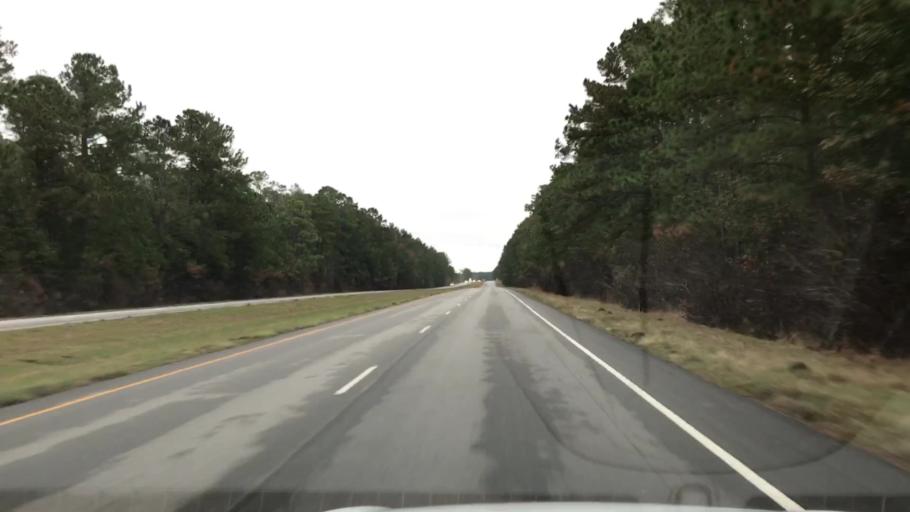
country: US
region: South Carolina
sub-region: Charleston County
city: Awendaw
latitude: 33.1639
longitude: -79.4239
